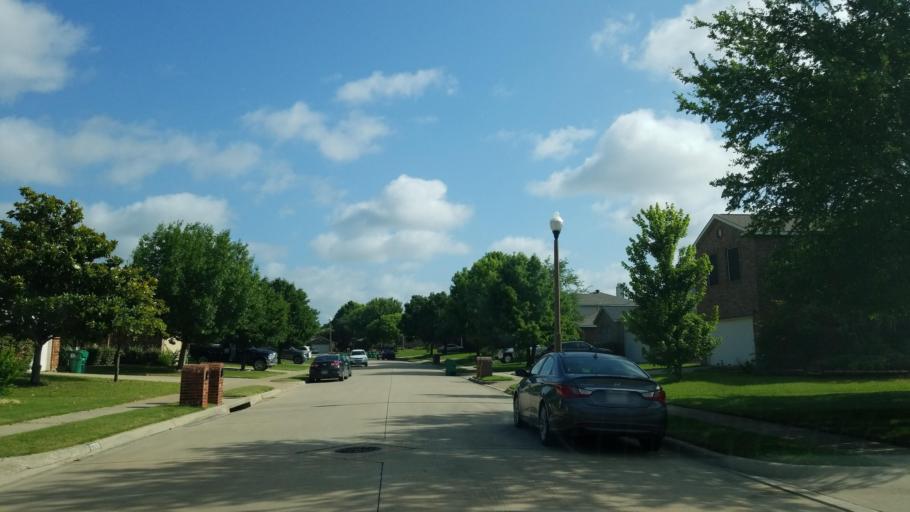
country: US
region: Texas
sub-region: Denton County
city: Copper Canyon
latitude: 33.1438
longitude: -97.1166
